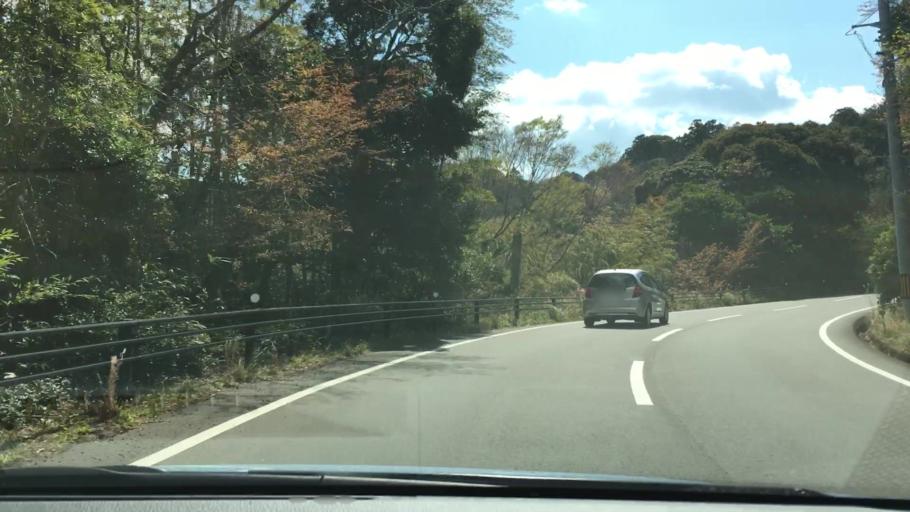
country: JP
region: Mie
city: Toba
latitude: 34.4420
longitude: 136.8883
